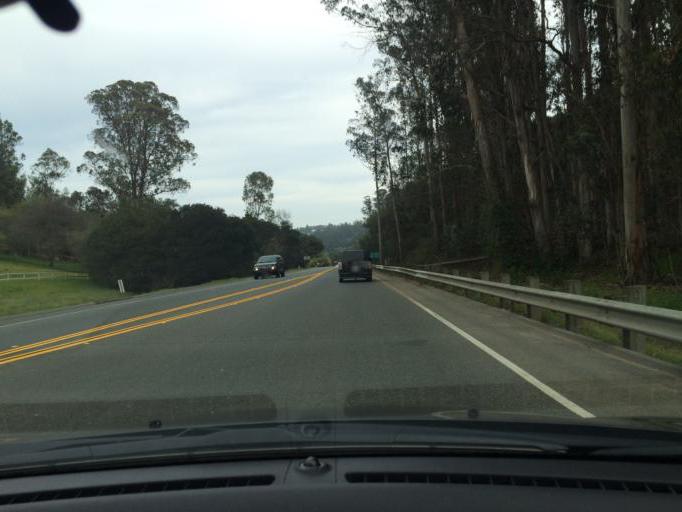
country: US
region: California
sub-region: Monterey County
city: Prunedale
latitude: 36.7882
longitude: -121.6785
